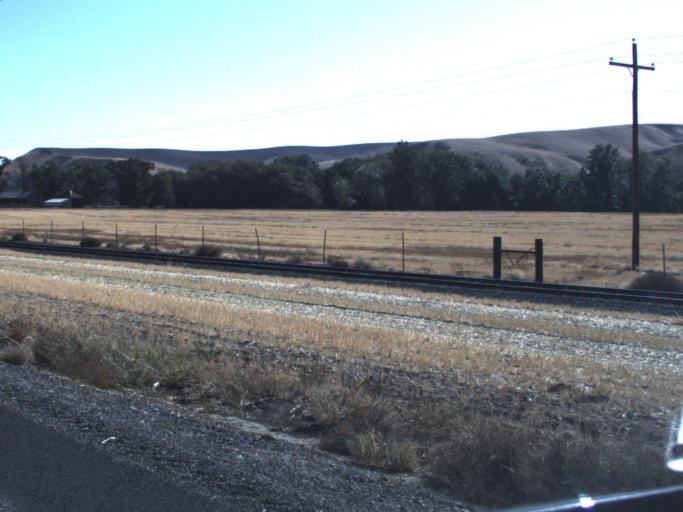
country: US
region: Washington
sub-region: Walla Walla County
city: Waitsburg
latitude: 46.2880
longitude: -118.2521
